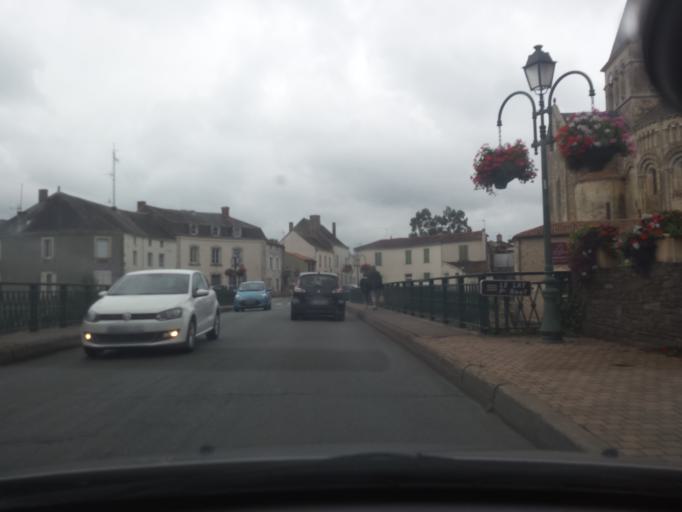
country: FR
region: Pays de la Loire
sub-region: Departement de la Vendee
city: Mareuil-sur-Lay-Dissais
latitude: 46.5350
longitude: -1.2198
